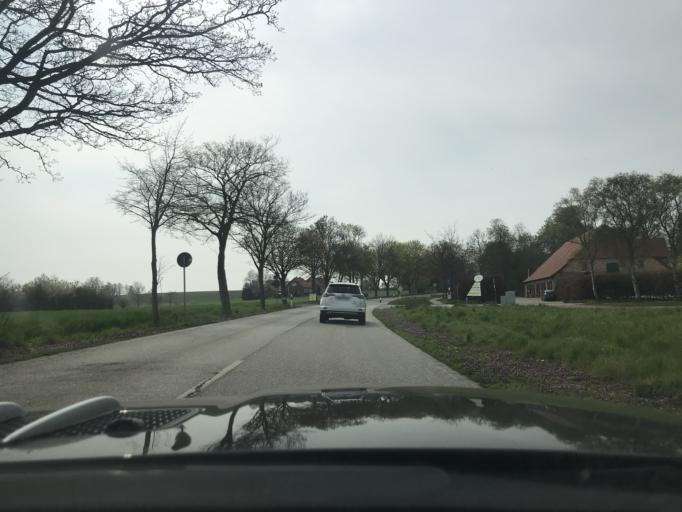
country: DE
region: Schleswig-Holstein
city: Heringsdorf
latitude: 54.2910
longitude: 11.0168
